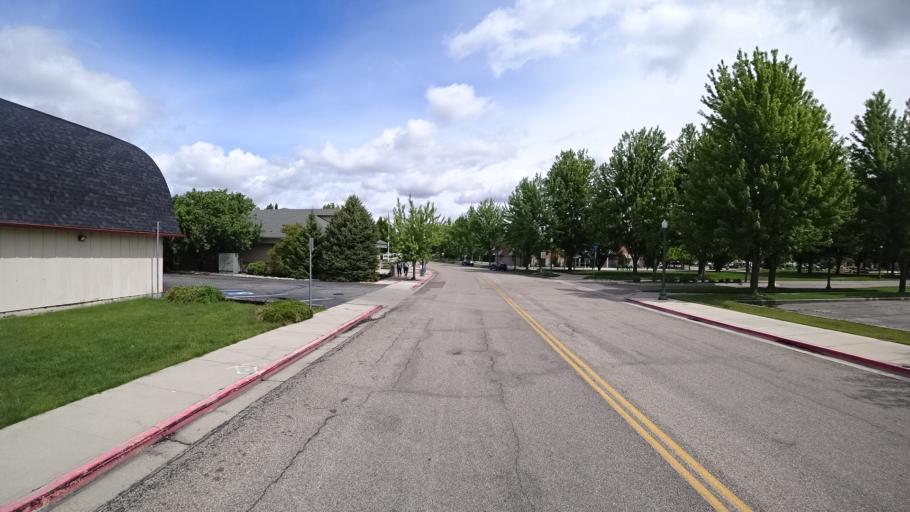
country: US
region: Idaho
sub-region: Ada County
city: Eagle
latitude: 43.6953
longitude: -116.3473
